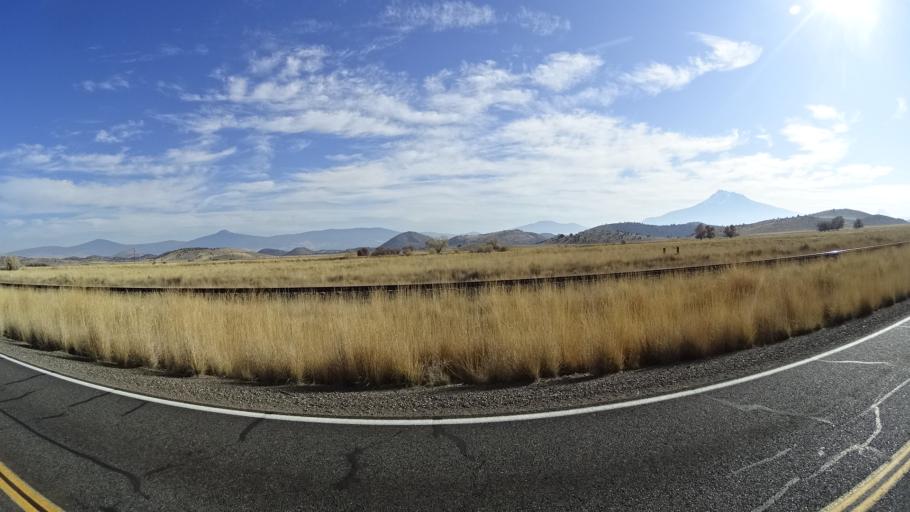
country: US
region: California
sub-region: Siskiyou County
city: Montague
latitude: 41.5989
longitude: -122.5237
